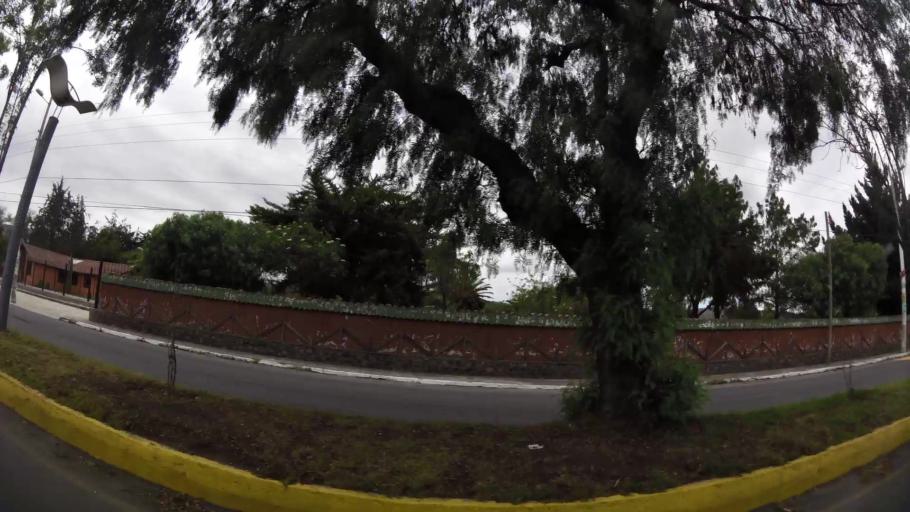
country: EC
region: Cotopaxi
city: San Miguel de Salcedo
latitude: -1.0360
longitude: -78.5907
